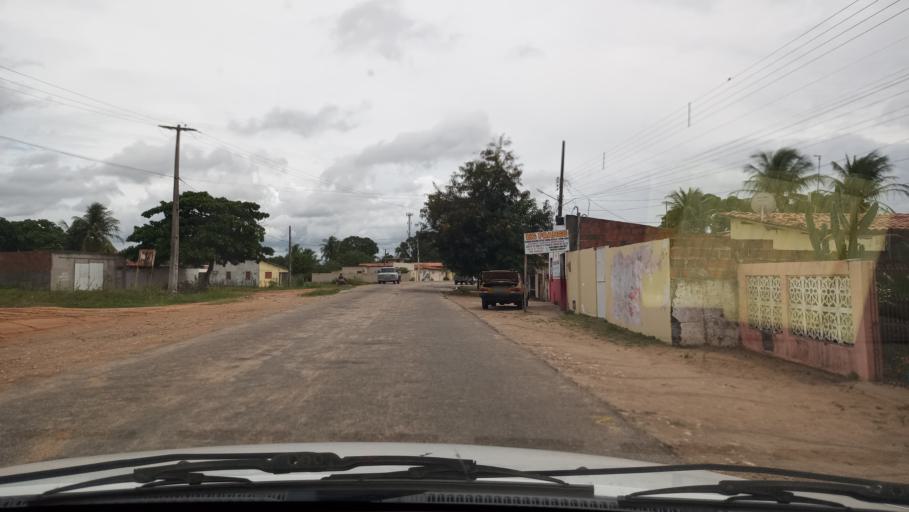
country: BR
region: Rio Grande do Norte
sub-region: Poco Branco
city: Poco Branco
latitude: -5.6179
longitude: -35.6540
